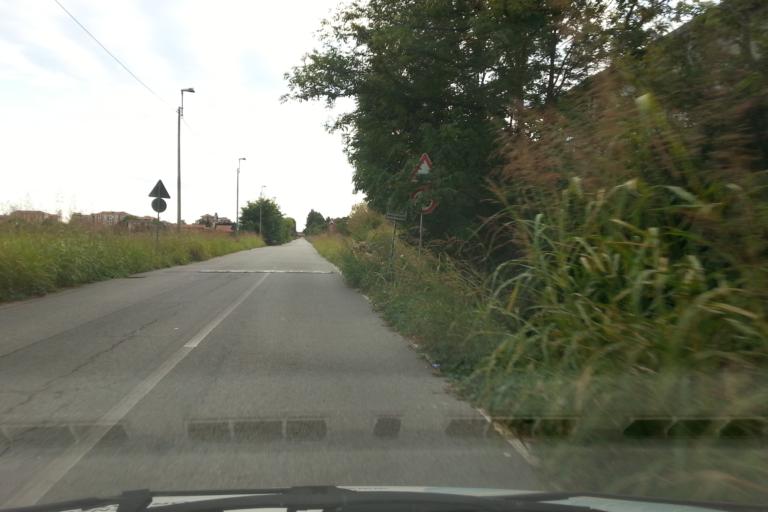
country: IT
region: Piedmont
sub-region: Provincia di Torino
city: Savonera
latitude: 45.1218
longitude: 7.6175
